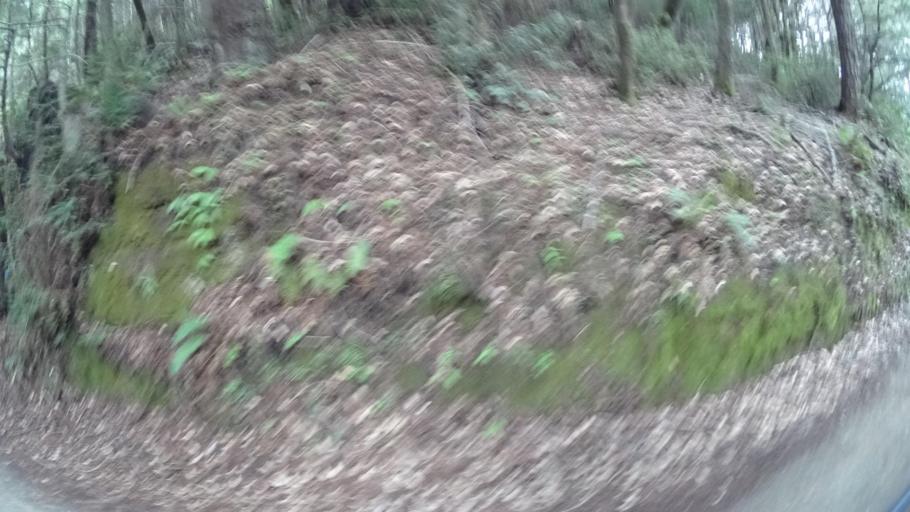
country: US
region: California
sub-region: Humboldt County
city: Redway
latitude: 40.3191
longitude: -123.8295
